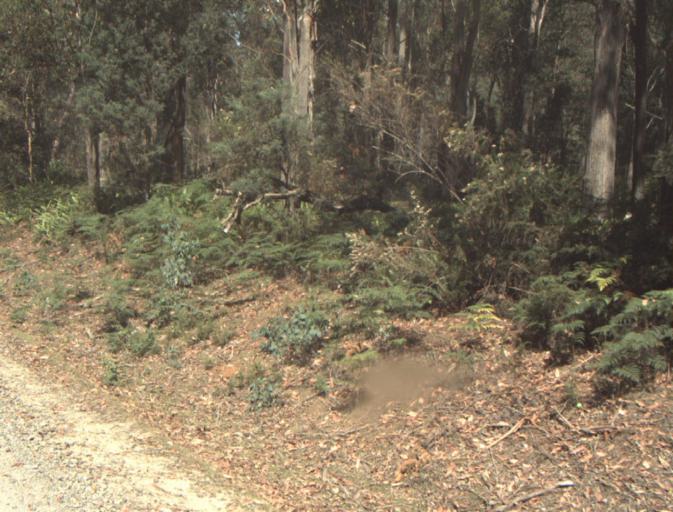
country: AU
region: Tasmania
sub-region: Dorset
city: Scottsdale
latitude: -41.3801
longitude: 147.4939
